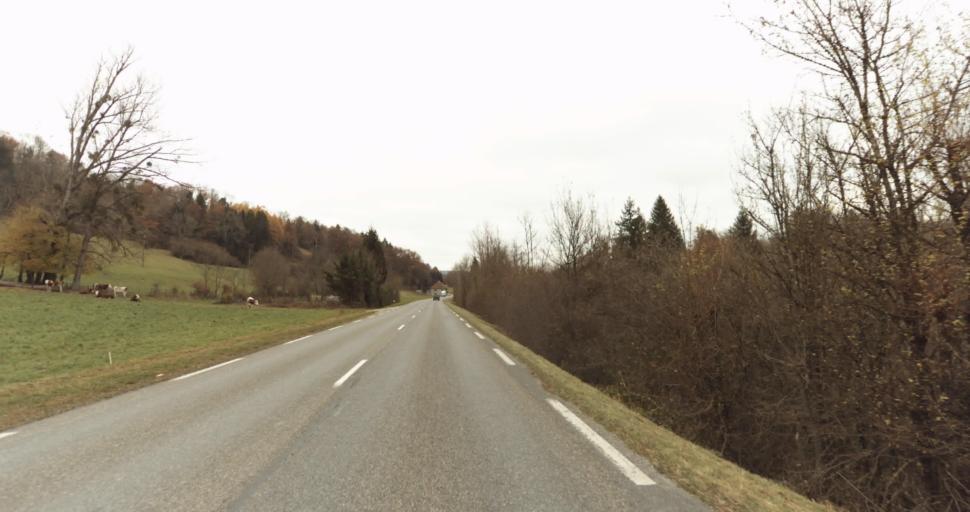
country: FR
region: Rhone-Alpes
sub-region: Departement de la Haute-Savoie
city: Groisy
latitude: 45.9898
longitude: 6.1705
